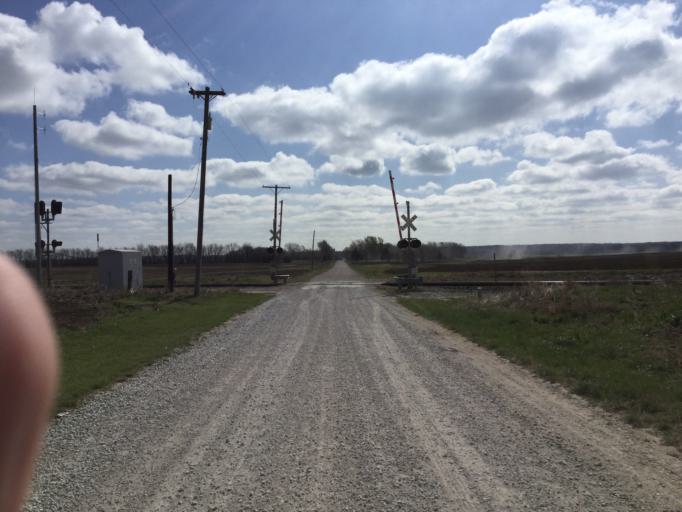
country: US
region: Kansas
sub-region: Wilson County
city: Neodesha
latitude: 37.3704
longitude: -95.6976
